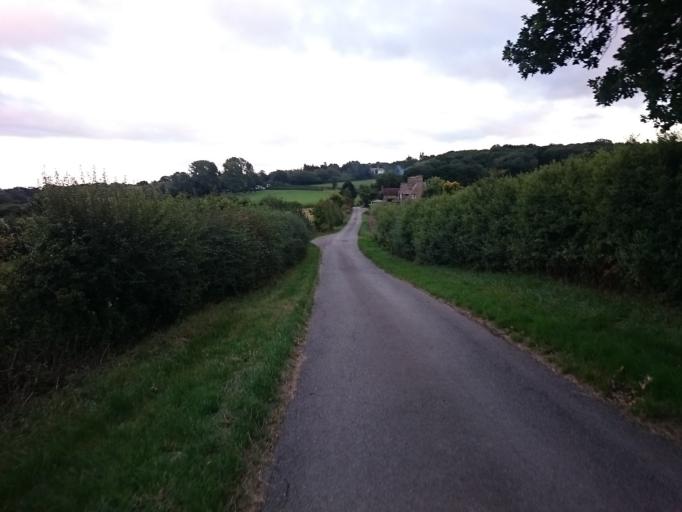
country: GB
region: England
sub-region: Oxfordshire
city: Boars Hill
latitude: 51.7243
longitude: -1.2819
